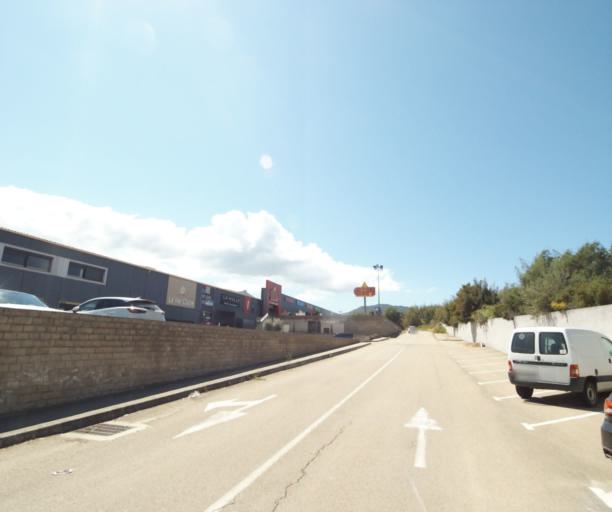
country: FR
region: Corsica
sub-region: Departement de la Corse-du-Sud
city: Propriano
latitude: 41.6687
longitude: 8.9180
